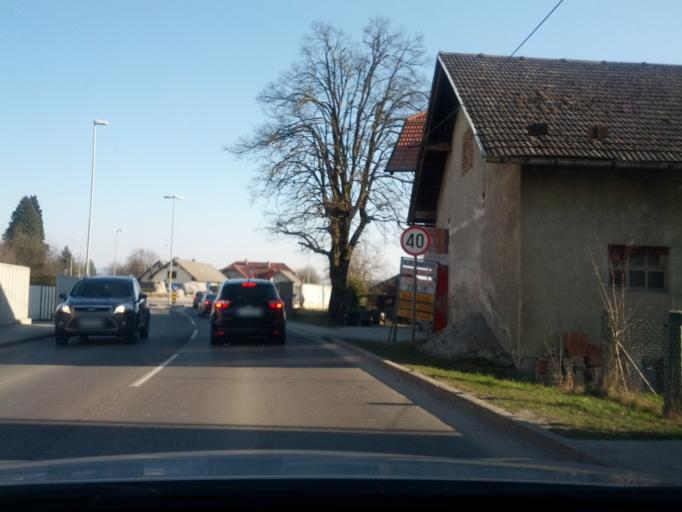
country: SI
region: Cerklje na Gorenjskem
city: Cerklje na Gorenjskem
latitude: 46.2289
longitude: 14.4838
